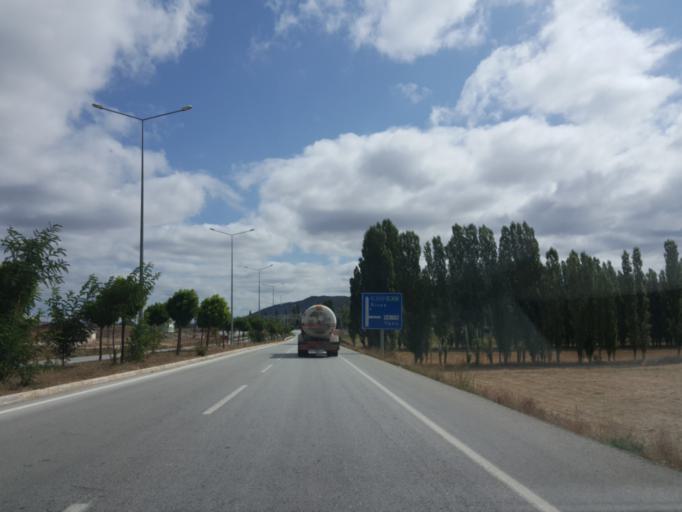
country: TR
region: Sivas
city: Yavu
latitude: 39.7967
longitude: 36.1978
